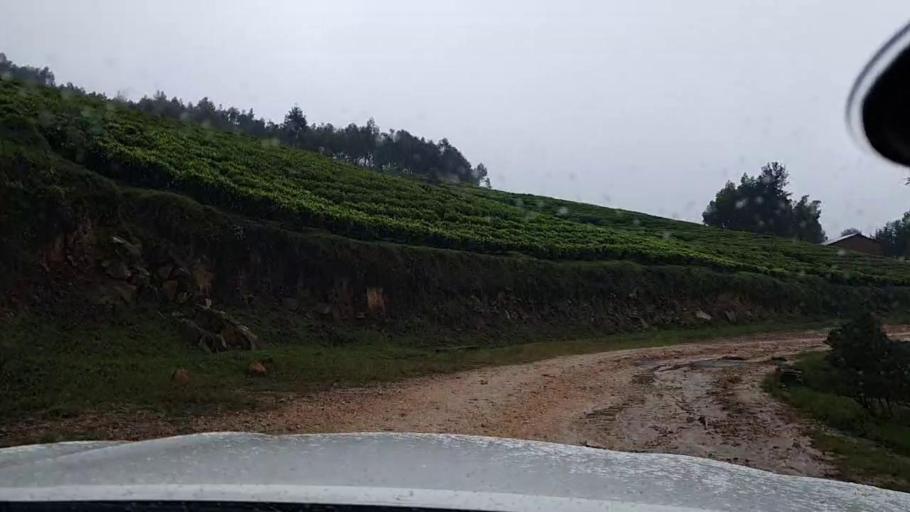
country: RW
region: Western Province
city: Kibuye
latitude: -2.1350
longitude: 29.4683
